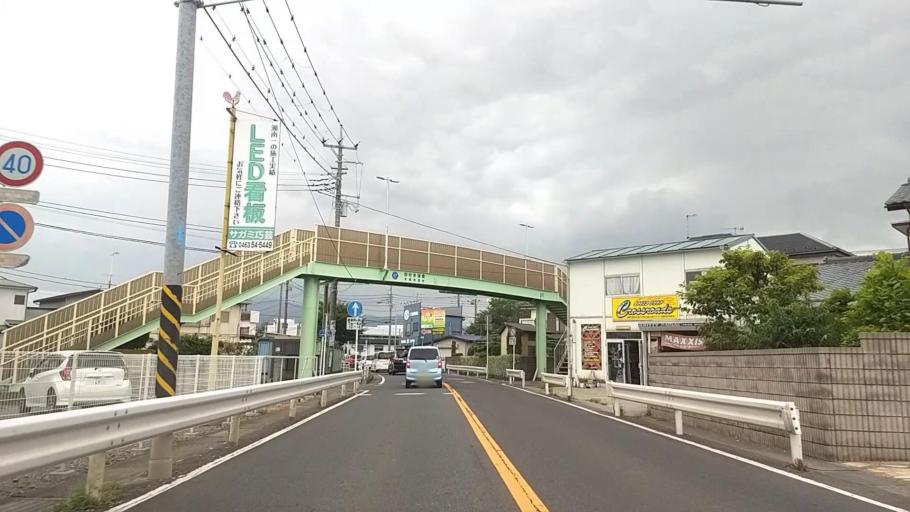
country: JP
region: Kanagawa
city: Hiratsuka
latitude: 35.3753
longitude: 139.3635
